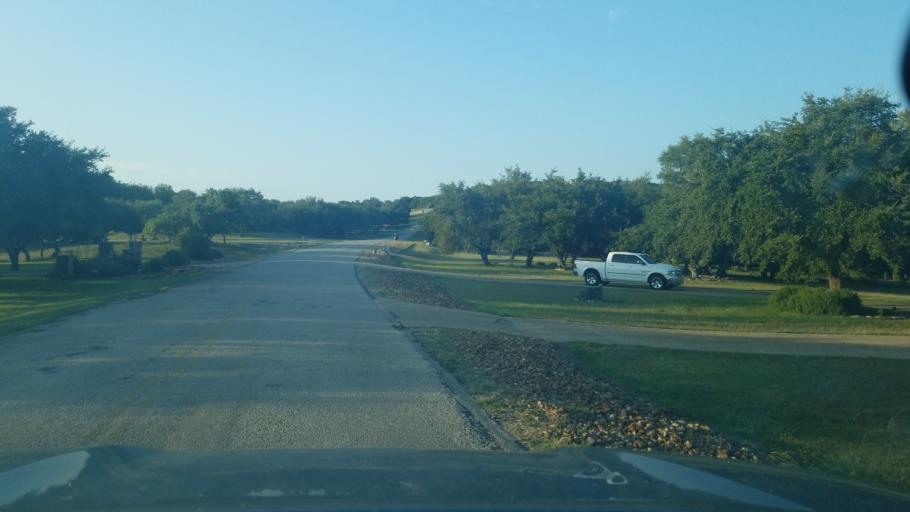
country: US
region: Texas
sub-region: Comal County
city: Bulverde
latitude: 29.8235
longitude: -98.4073
